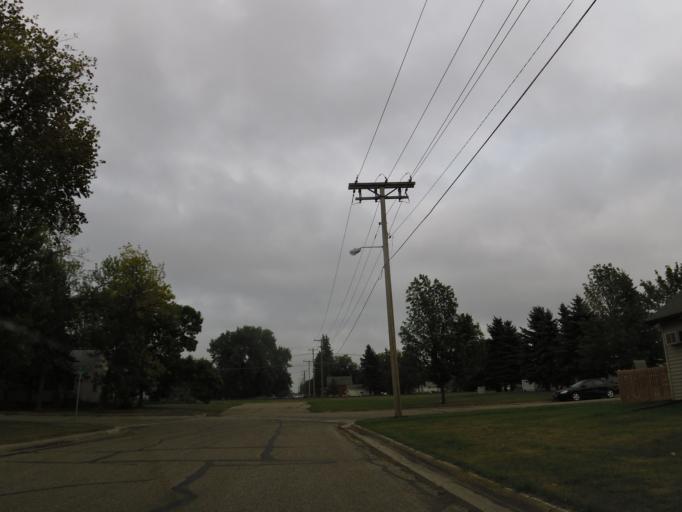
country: US
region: North Dakota
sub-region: Walsh County
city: Grafton
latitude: 48.5581
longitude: -97.1810
